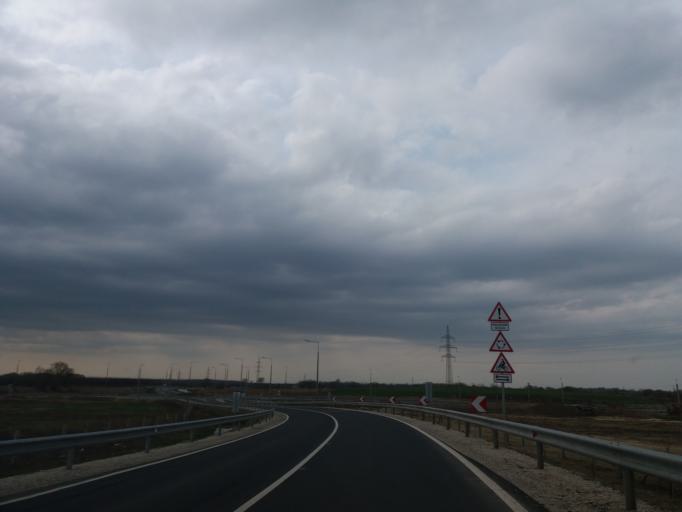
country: HU
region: Szabolcs-Szatmar-Bereg
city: Kisvarda
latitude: 48.2018
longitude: 22.0700
